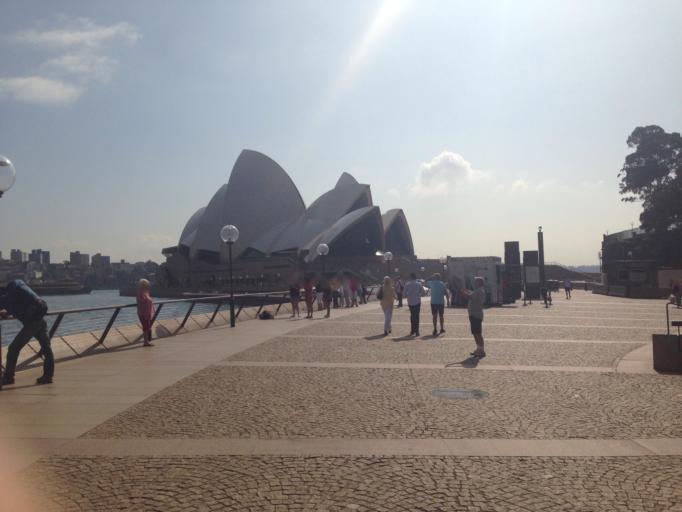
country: AU
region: New South Wales
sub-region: City of Sydney
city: Sydney
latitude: -33.8589
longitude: 151.2131
